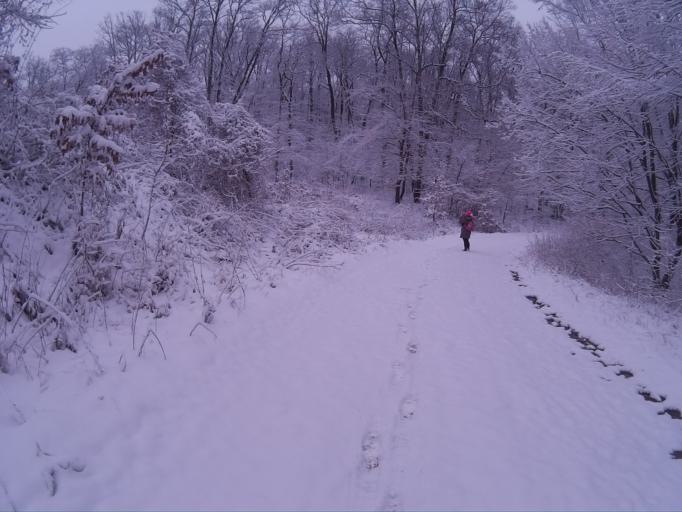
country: HU
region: Komarom-Esztergom
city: Tarjan
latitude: 47.5733
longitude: 18.5157
